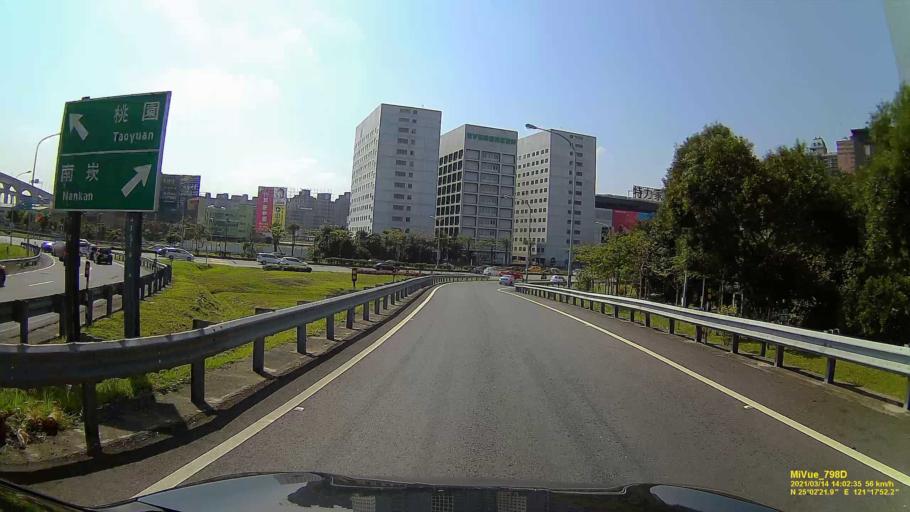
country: TW
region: Taiwan
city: Taoyuan City
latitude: 25.0400
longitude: 121.2975
